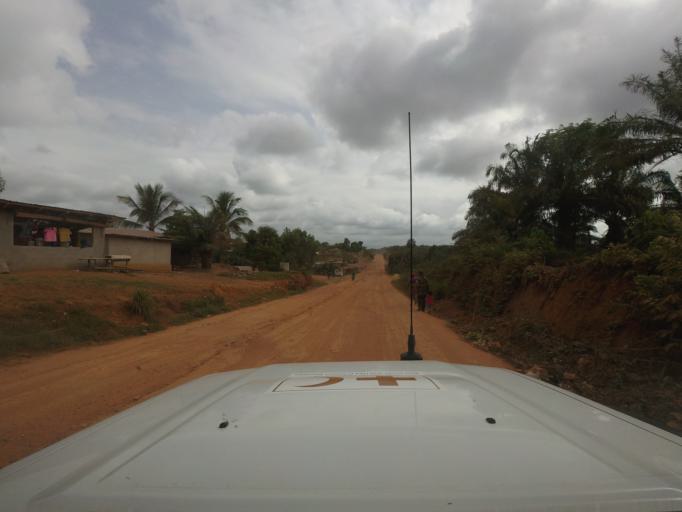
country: LR
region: Bong
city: Gbarnga
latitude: 7.0141
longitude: -9.4764
